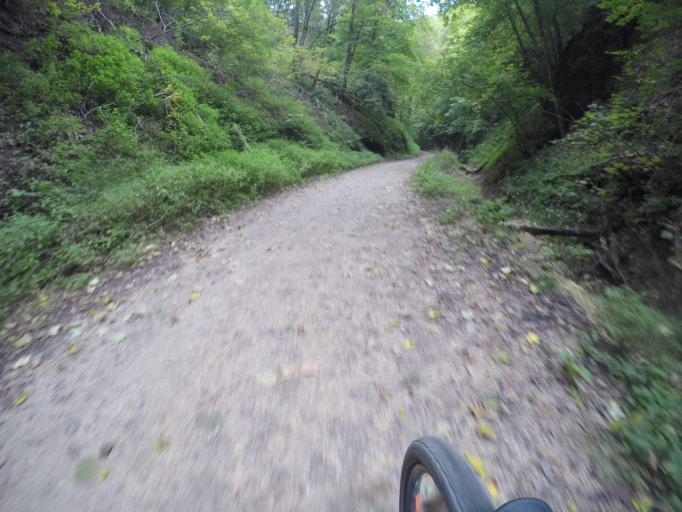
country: DE
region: Baden-Wuerttemberg
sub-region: Tuebingen Region
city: Munsingen
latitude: 48.4395
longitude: 9.4780
